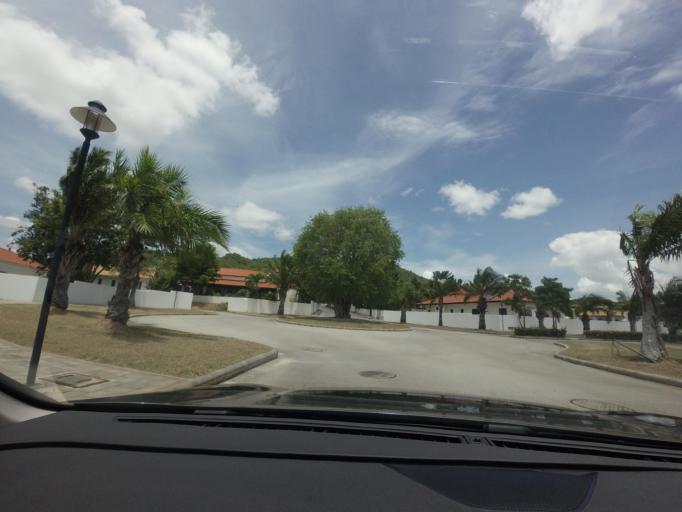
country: TH
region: Prachuap Khiri Khan
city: Hua Hin
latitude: 12.5156
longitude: 99.9602
